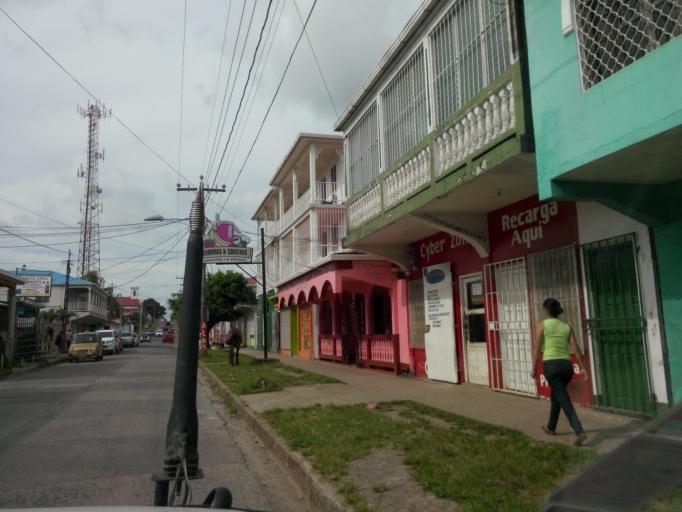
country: NI
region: Atlantico Sur
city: Bluefields
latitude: 12.0121
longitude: -83.7632
